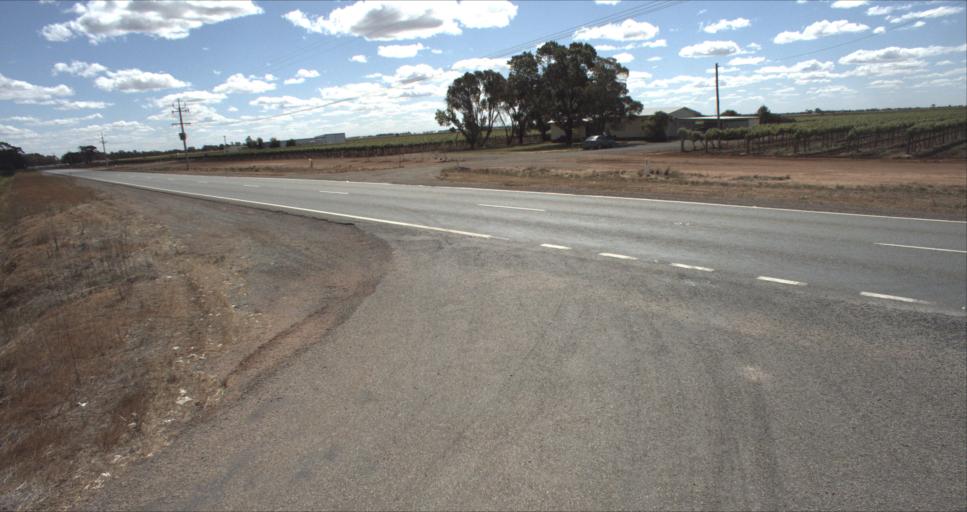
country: AU
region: New South Wales
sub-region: Leeton
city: Leeton
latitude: -34.5052
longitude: 146.2213
